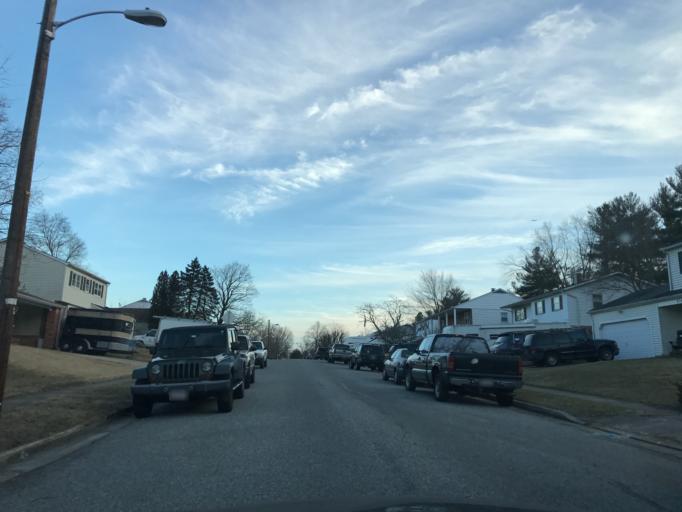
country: US
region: Maryland
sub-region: Harford County
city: Joppatowne
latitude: 39.4169
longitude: -76.3677
